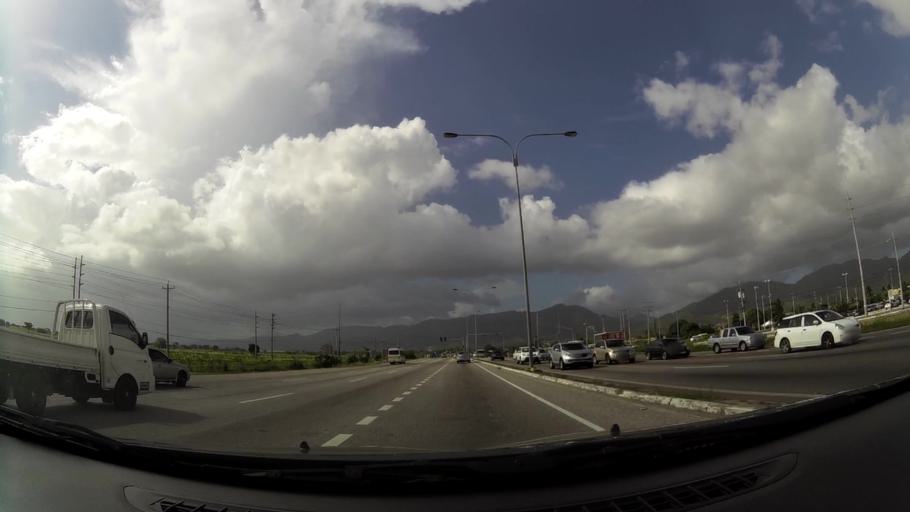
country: TT
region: Tunapuna/Piarco
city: Arouca
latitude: 10.6246
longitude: -61.3563
